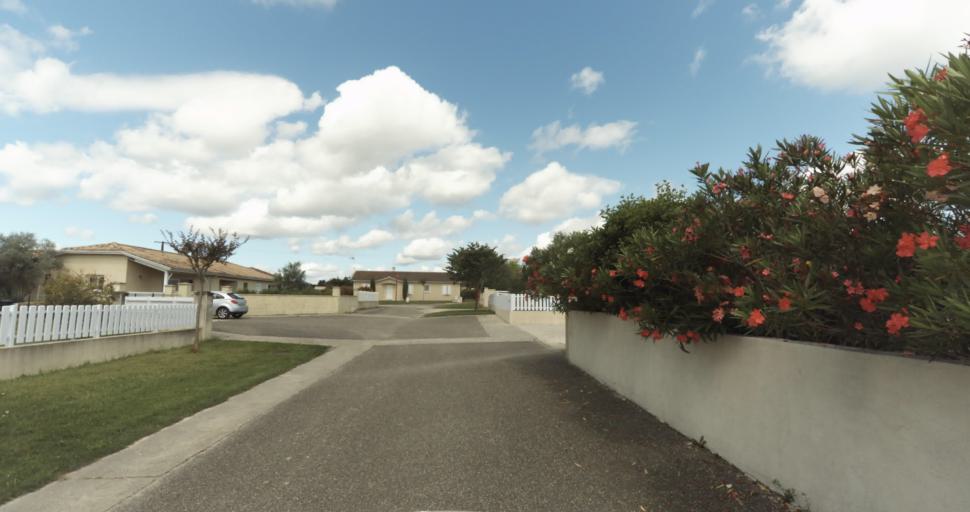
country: FR
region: Aquitaine
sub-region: Departement de la Gironde
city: Bazas
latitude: 44.4403
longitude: -0.2053
